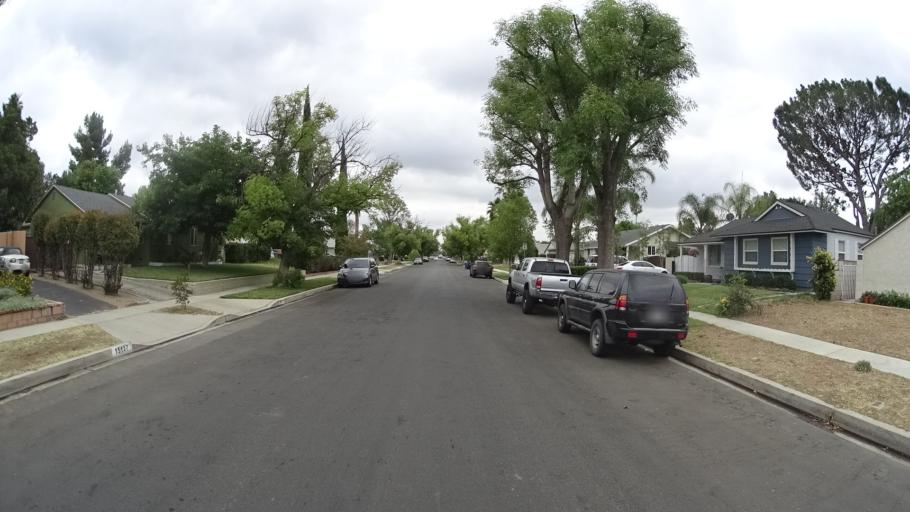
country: US
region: California
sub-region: Los Angeles County
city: San Fernando
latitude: 34.2601
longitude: -118.4623
